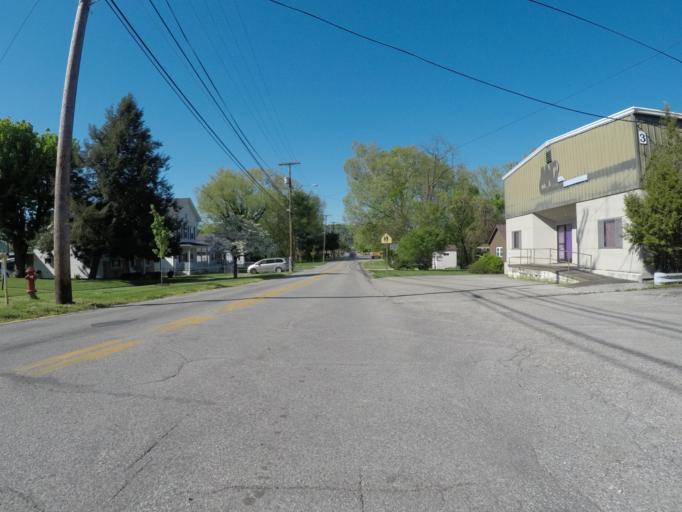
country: US
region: West Virginia
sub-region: Wayne County
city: Ceredo
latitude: 38.3926
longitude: -82.5595
